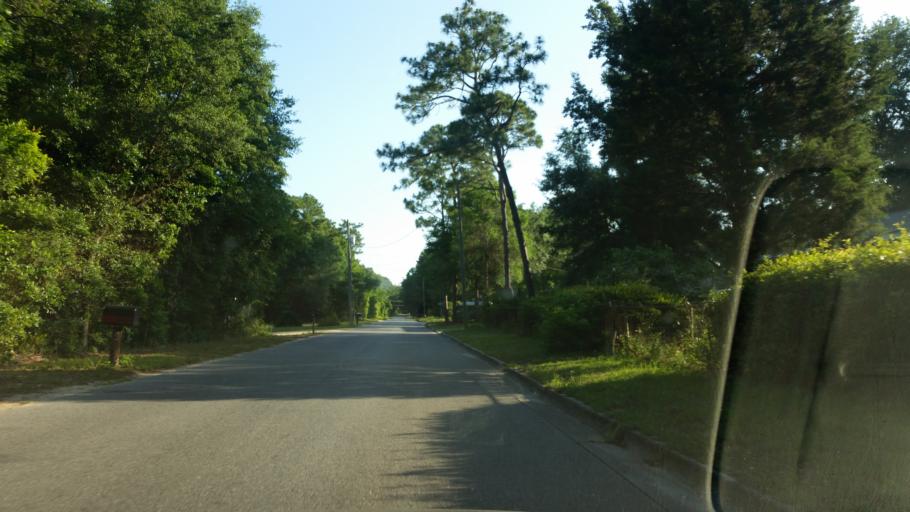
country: US
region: Florida
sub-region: Escambia County
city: Ferry Pass
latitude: 30.5332
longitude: -87.2162
